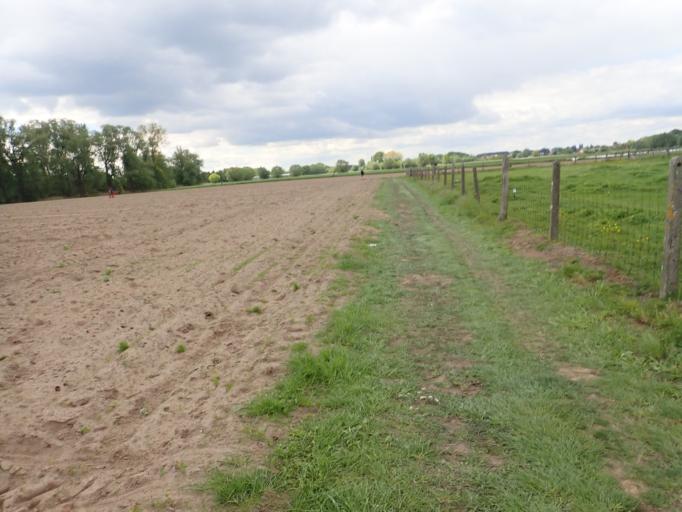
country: BE
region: Flanders
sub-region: Provincie Oost-Vlaanderen
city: Lebbeke
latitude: 51.0050
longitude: 4.1189
